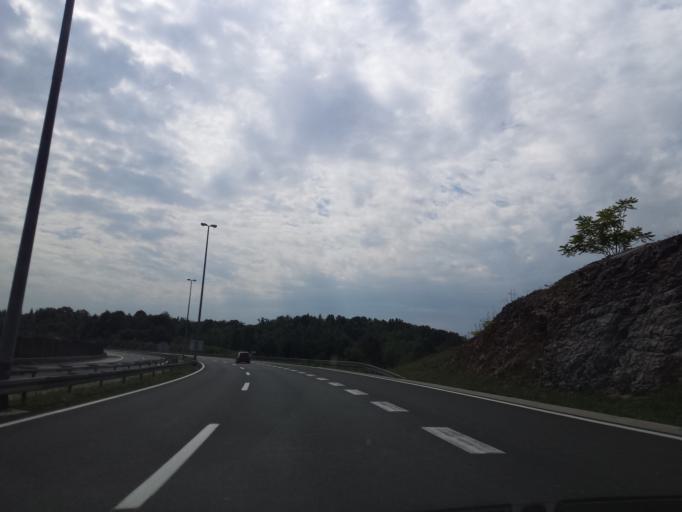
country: HR
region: Karlovacka
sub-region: Grad Ogulin
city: Ogulin
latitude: 45.4020
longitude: 15.2495
